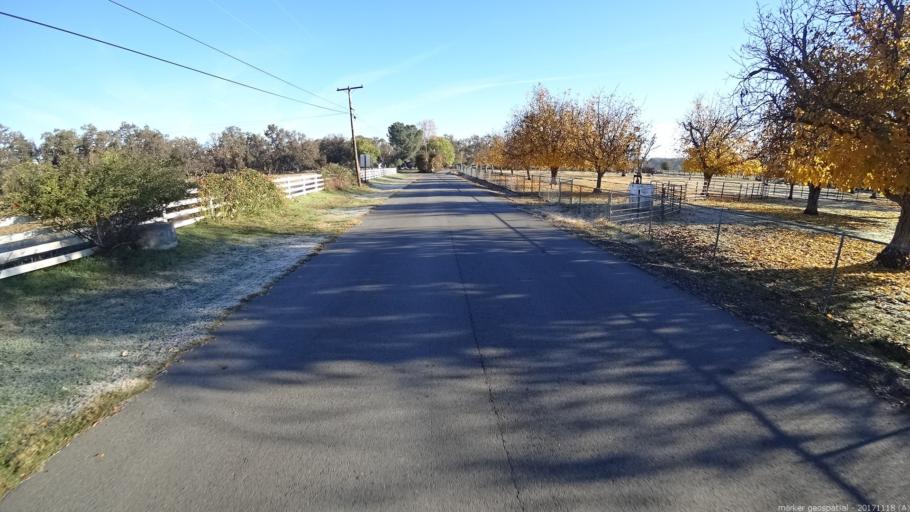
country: US
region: California
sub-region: Shasta County
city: Anderson
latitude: 40.4587
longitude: -122.2516
